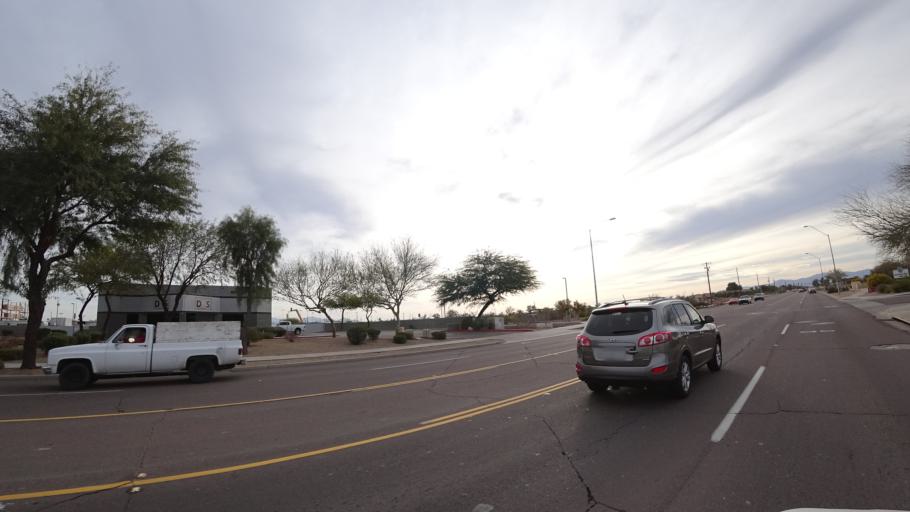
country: US
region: Arizona
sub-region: Maricopa County
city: Peoria
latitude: 33.5666
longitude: -112.2327
